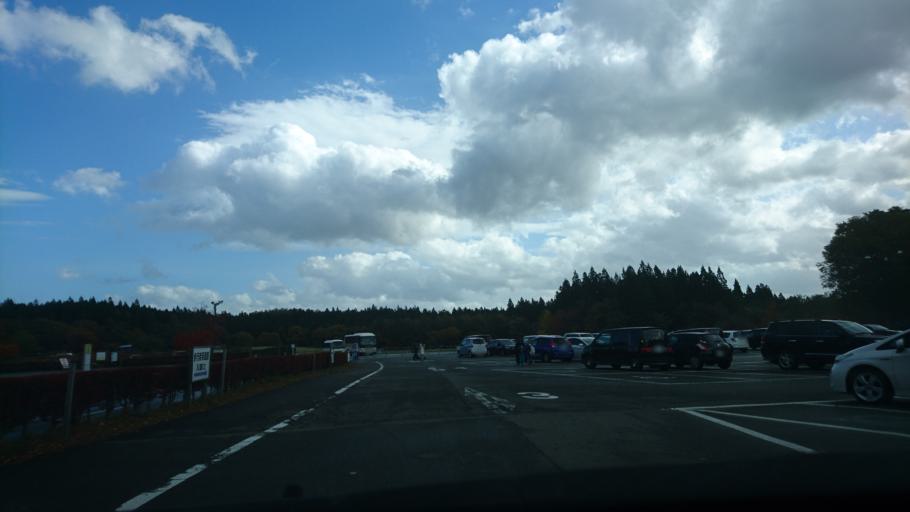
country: JP
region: Iwate
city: Shizukuishi
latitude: 39.7504
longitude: 141.0165
